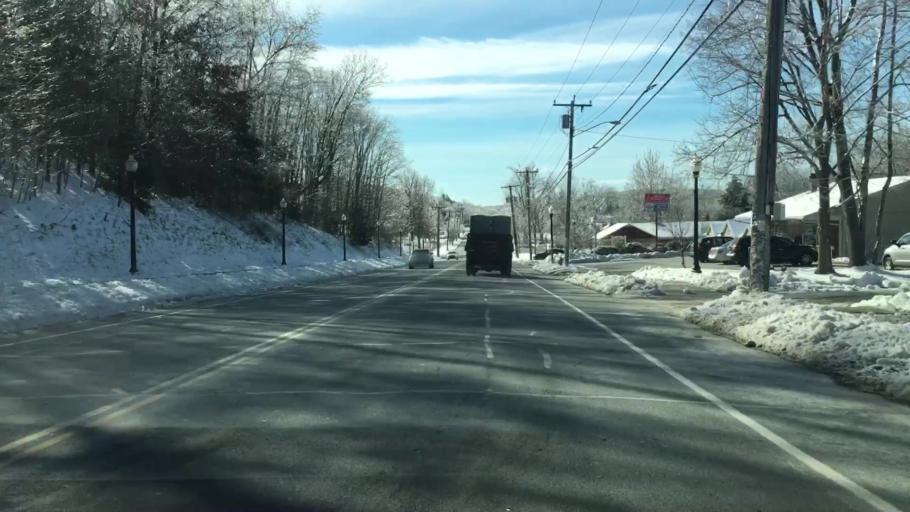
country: US
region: Connecticut
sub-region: New Haven County
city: Southbury
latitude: 41.4741
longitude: -73.2205
